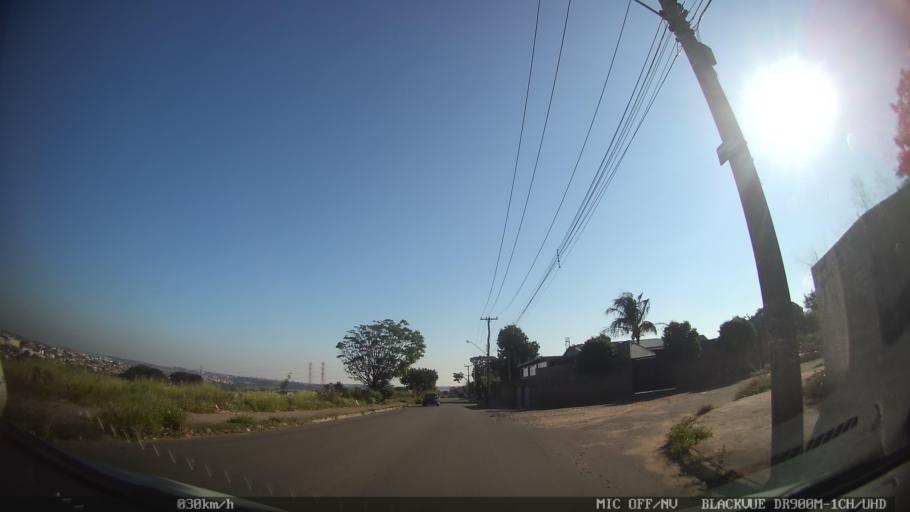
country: BR
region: Sao Paulo
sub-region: Campinas
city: Campinas
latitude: -22.9773
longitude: -47.1097
